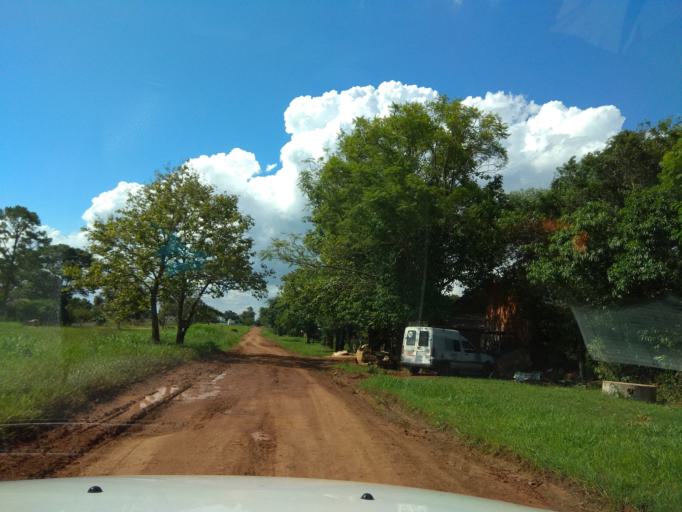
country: AR
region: Misiones
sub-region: Departamento de Candelaria
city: Candelaria
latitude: -27.4583
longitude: -55.7547
